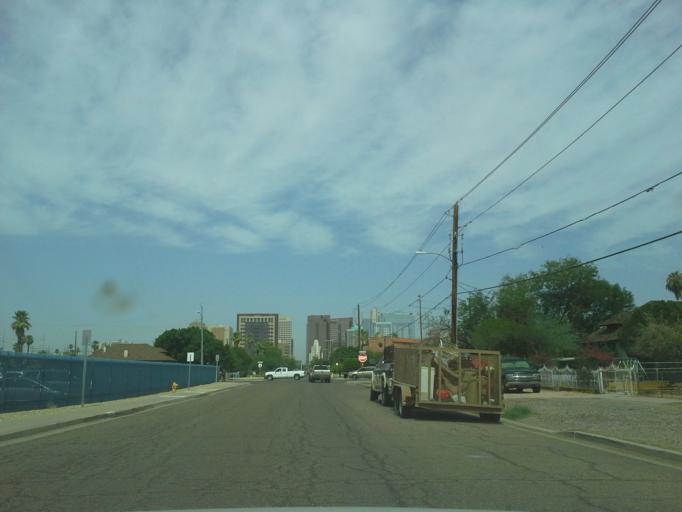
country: US
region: Arizona
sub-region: Maricopa County
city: Phoenix
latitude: 33.4362
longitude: -112.0751
